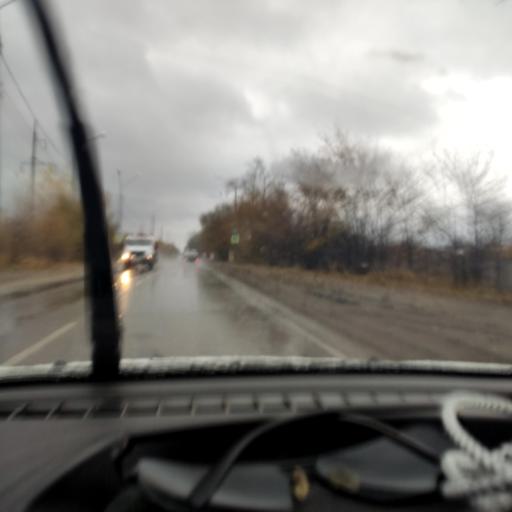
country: RU
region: Samara
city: Zhigulevsk
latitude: 53.4638
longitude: 49.5543
